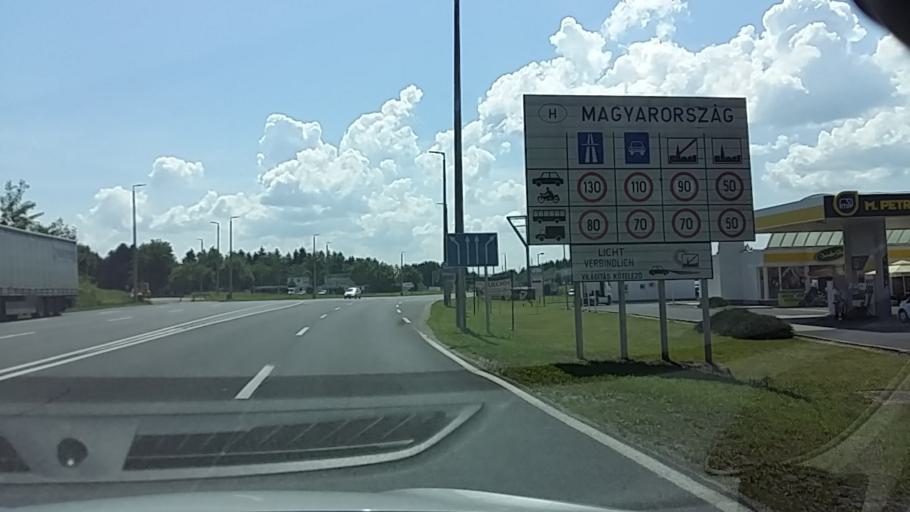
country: AT
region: Burgenland
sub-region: Politischer Bezirk Jennersdorf
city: Heiligenkreuz im Lafnitztal
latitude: 46.9829
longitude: 16.2804
